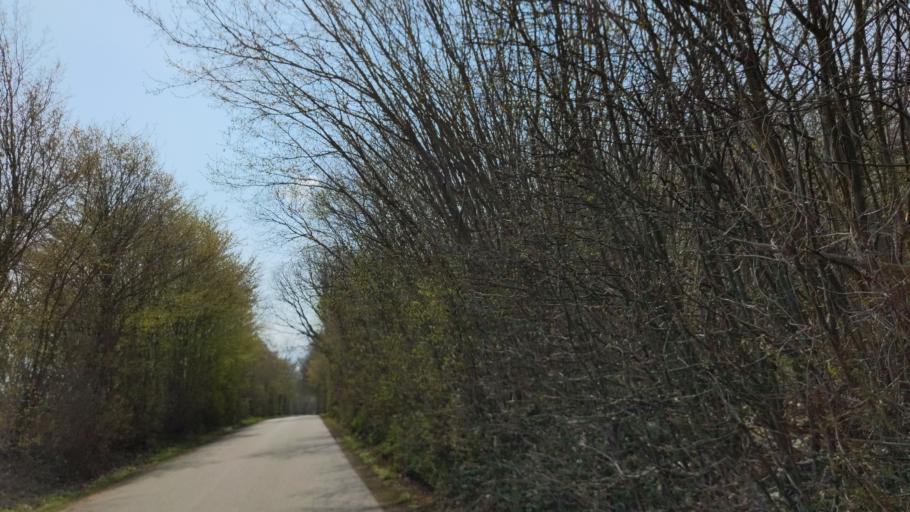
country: DE
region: Schleswig-Holstein
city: Timmendorfer Strand
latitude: 53.9342
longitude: 10.8041
